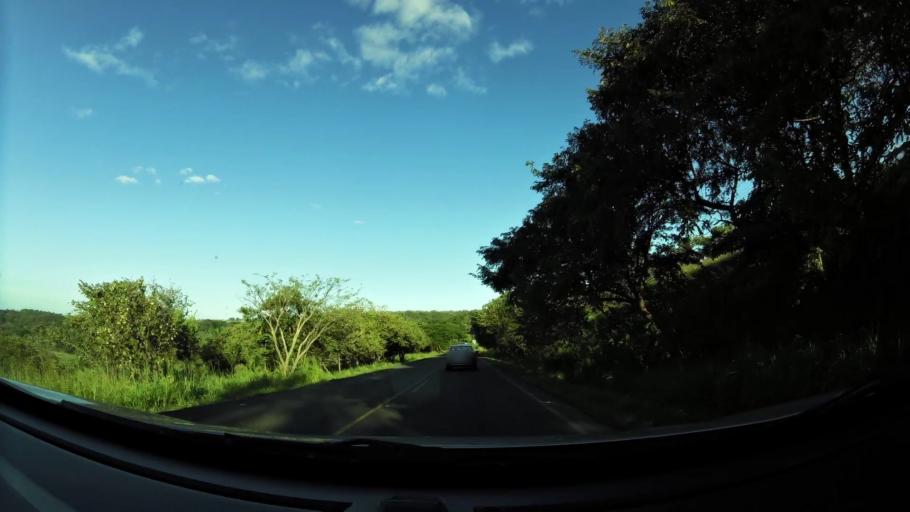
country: CR
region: Puntarenas
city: Miramar
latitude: 10.0989
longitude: -84.8038
